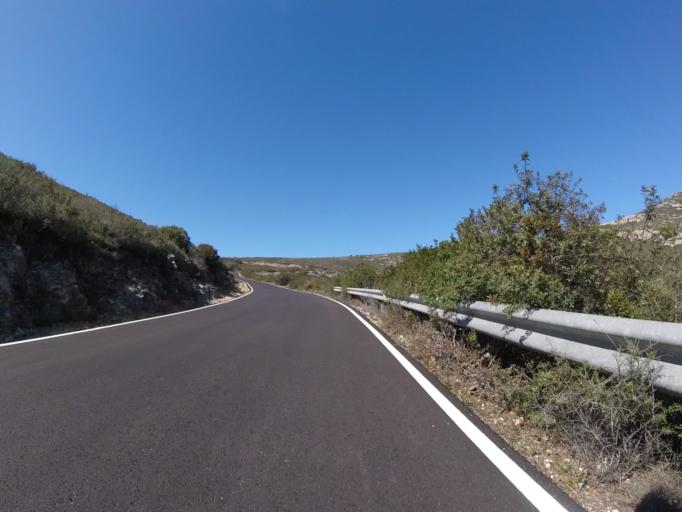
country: ES
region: Valencia
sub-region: Provincia de Castello
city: Cervera del Maestre
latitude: 40.4067
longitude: 0.2243
